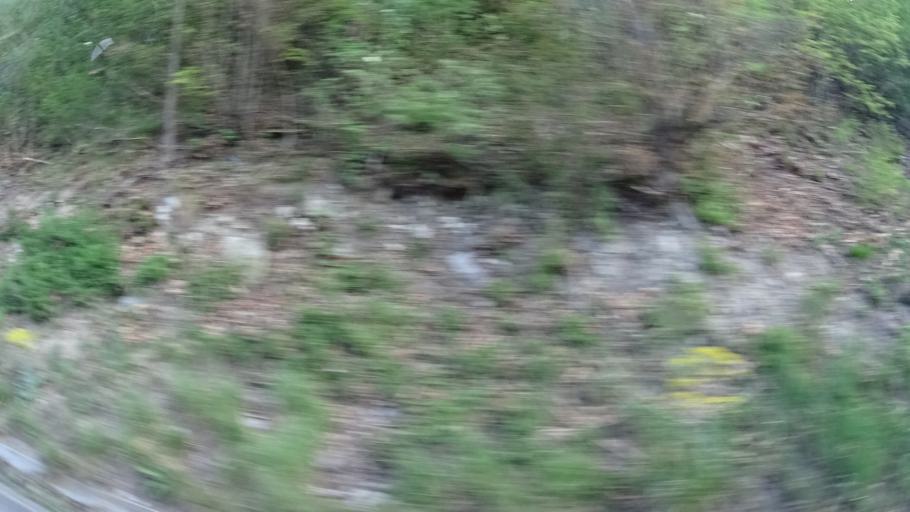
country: DE
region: Baden-Wuerttemberg
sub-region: Tuebingen Region
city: Haigerloch
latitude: 48.3985
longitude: 8.7807
